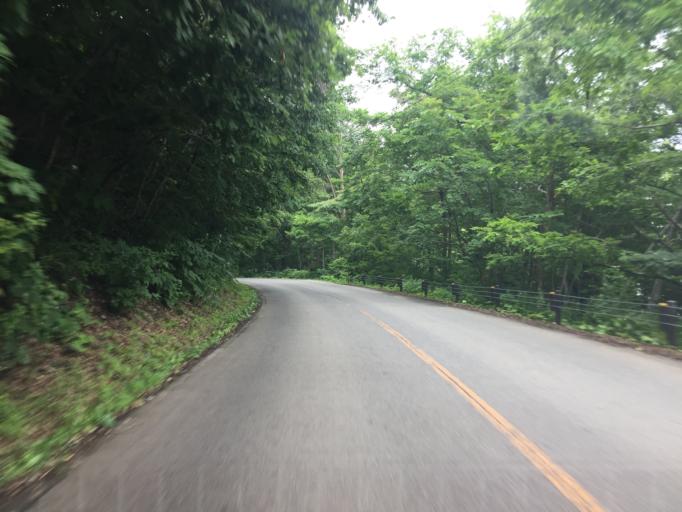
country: JP
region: Fukushima
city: Inawashiro
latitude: 37.7154
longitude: 140.0617
